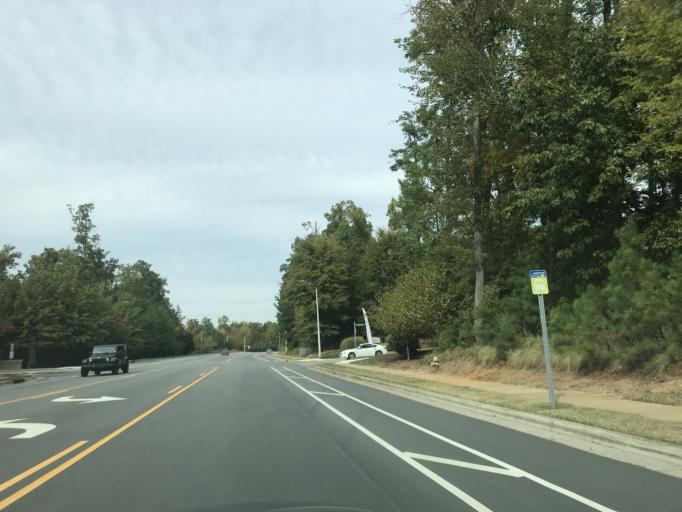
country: US
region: North Carolina
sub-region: Wake County
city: Wake Forest
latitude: 35.9515
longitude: -78.5456
